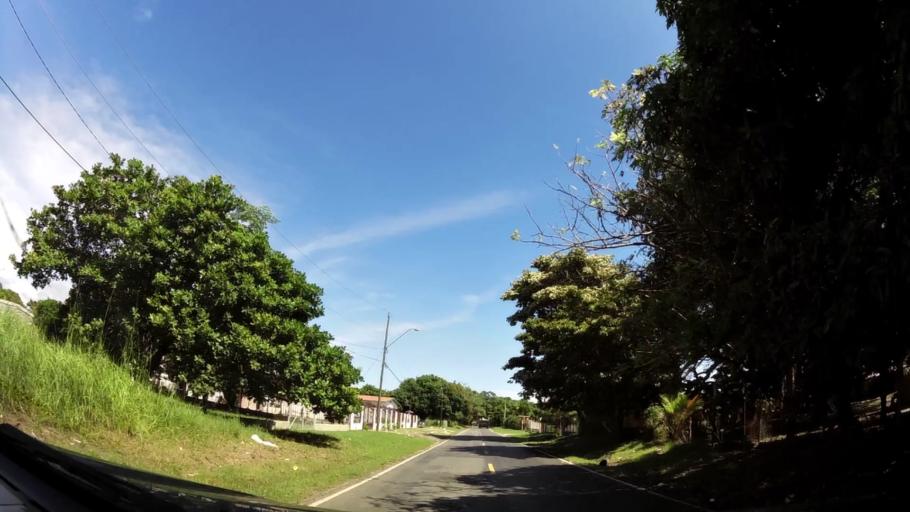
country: PA
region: Panama
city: Nueva Gorgona
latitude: 8.5577
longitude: -79.8726
